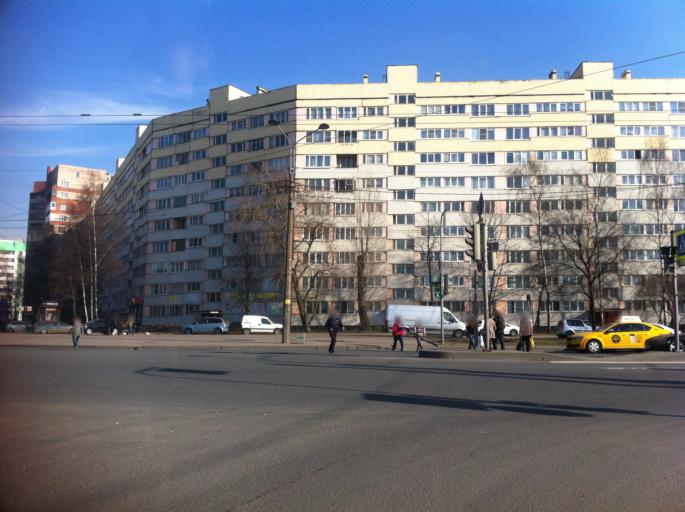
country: RU
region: St.-Petersburg
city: Dachnoye
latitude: 59.8596
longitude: 30.2322
